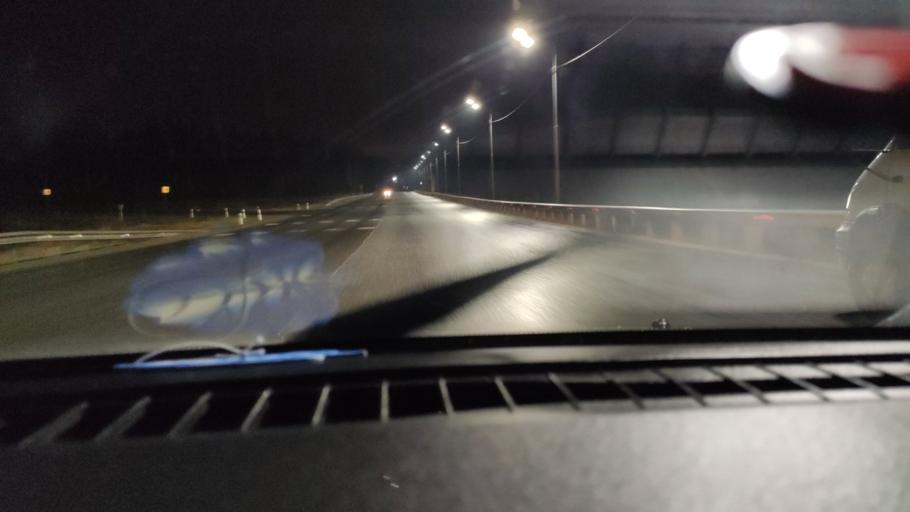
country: RU
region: Udmurtiya
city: Khokhryaki
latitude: 56.9157
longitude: 53.4527
